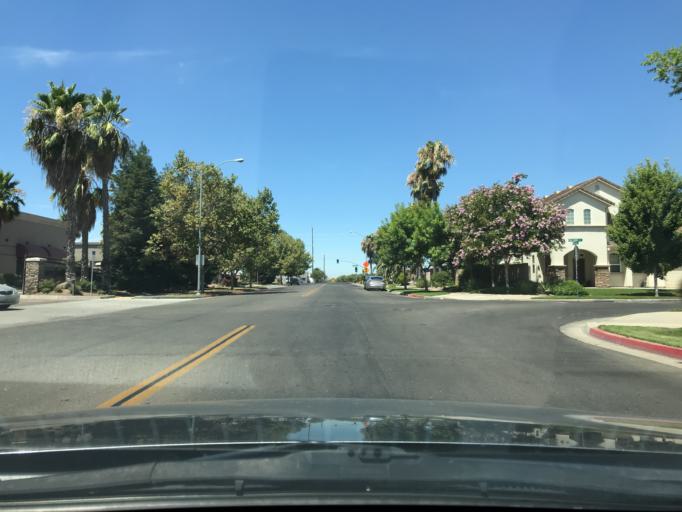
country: US
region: California
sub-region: Merced County
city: Merced
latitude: 37.3263
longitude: -120.5027
